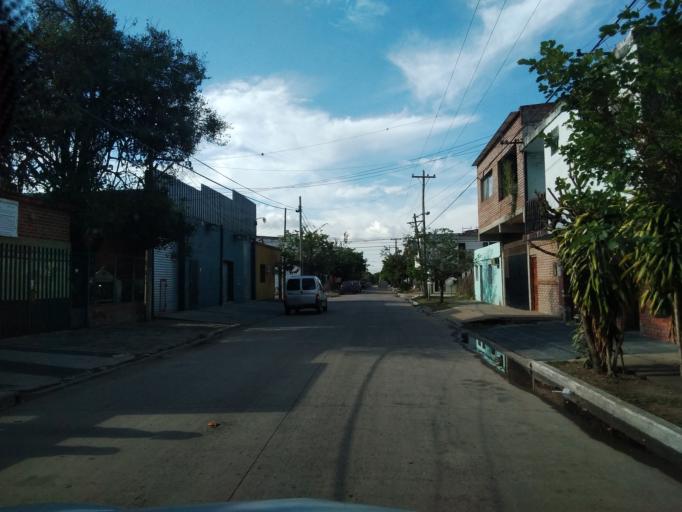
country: AR
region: Corrientes
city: Corrientes
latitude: -27.4652
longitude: -58.8140
